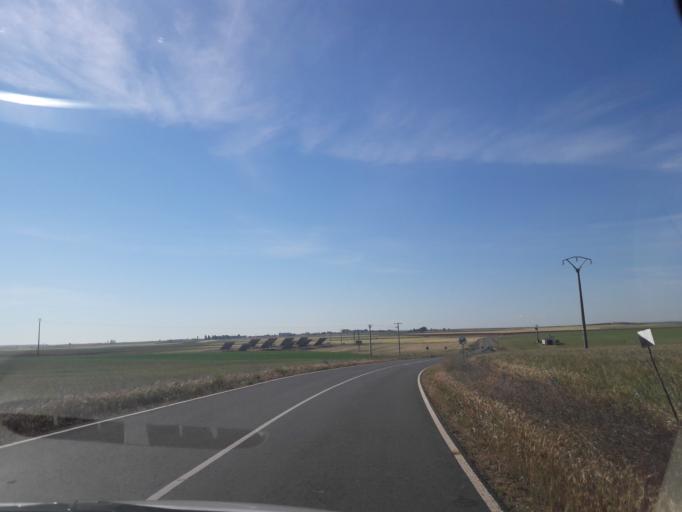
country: ES
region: Castille and Leon
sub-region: Provincia de Salamanca
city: Espino de la Orbada
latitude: 41.1017
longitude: -5.4189
